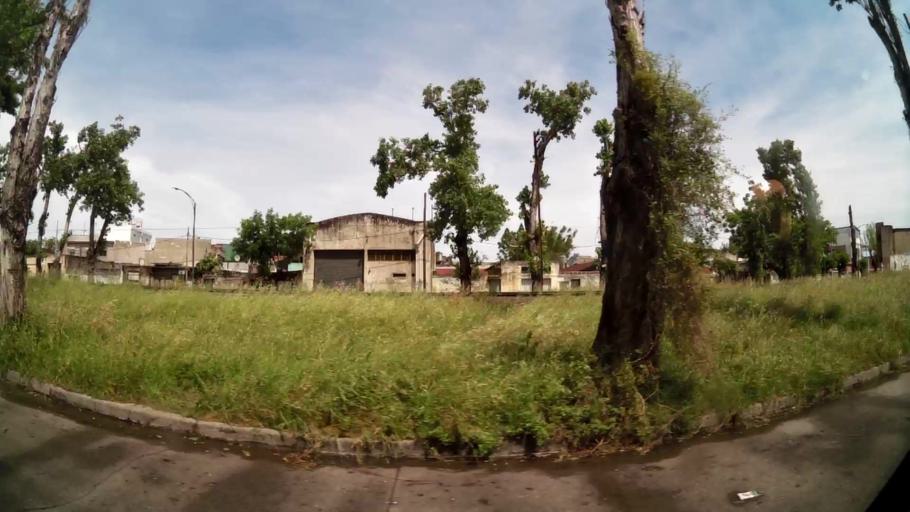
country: AR
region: Buenos Aires F.D.
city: Villa Lugano
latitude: -34.6613
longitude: -58.4390
